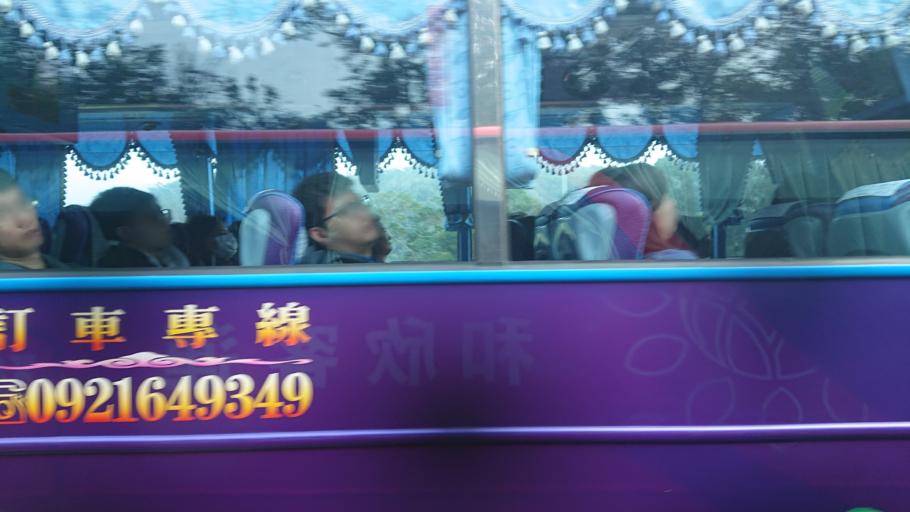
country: TW
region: Taiwan
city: Fengyuan
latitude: 24.3621
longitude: 120.7396
